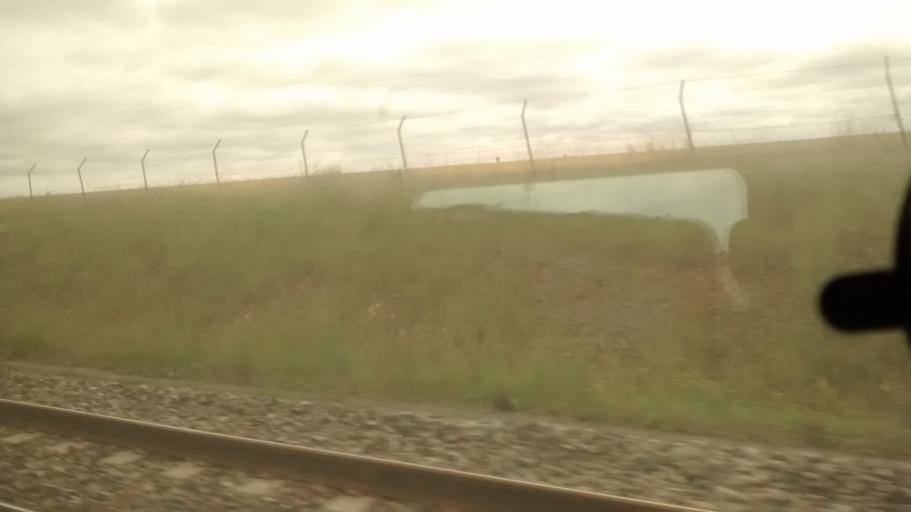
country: FR
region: Centre
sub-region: Departement d'Eure-et-Loir
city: Auneau
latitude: 48.4382
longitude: 1.7746
